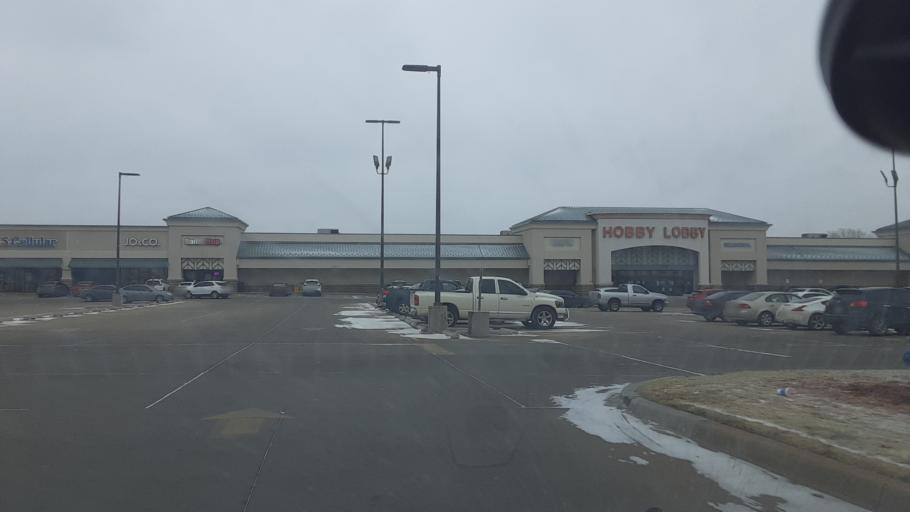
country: US
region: Oklahoma
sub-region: Payne County
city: Stillwater
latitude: 36.1278
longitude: -97.0509
